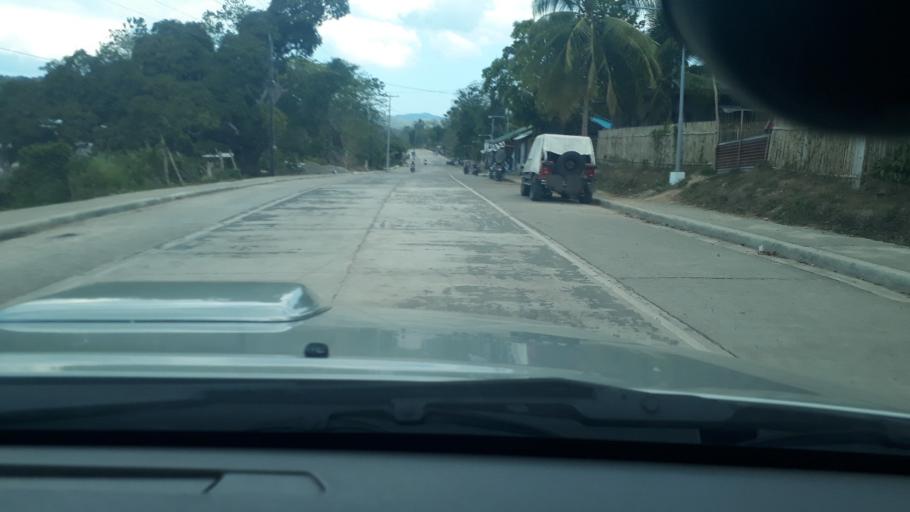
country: PH
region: Mimaropa
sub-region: Province of Palawan
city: Salvacion
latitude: 12.1336
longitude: 119.9371
